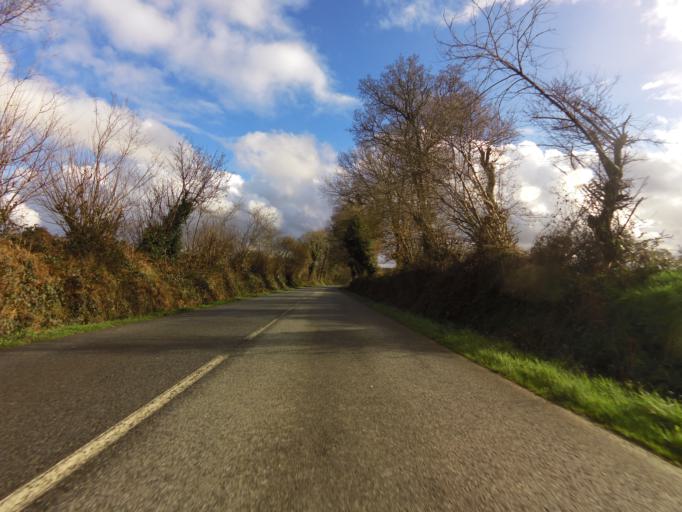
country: FR
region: Brittany
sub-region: Departement du Morbihan
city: Gourin
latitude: 48.1474
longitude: -3.6212
